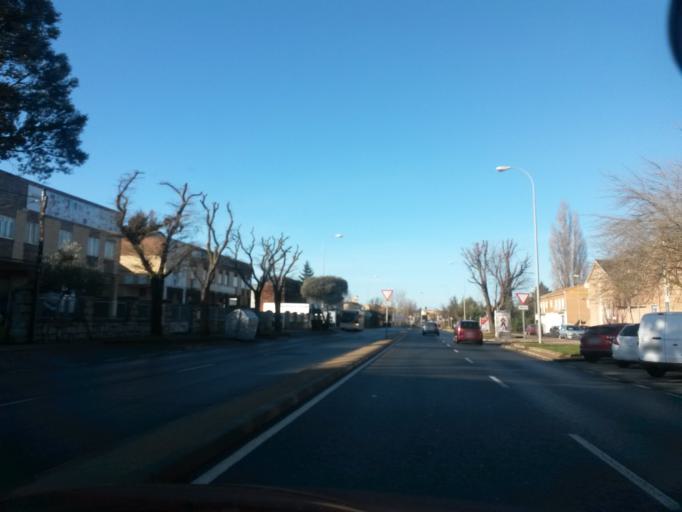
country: ES
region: Castille and Leon
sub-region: Provincia de Salamanca
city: Salamanca
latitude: 40.9549
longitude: -5.6887
